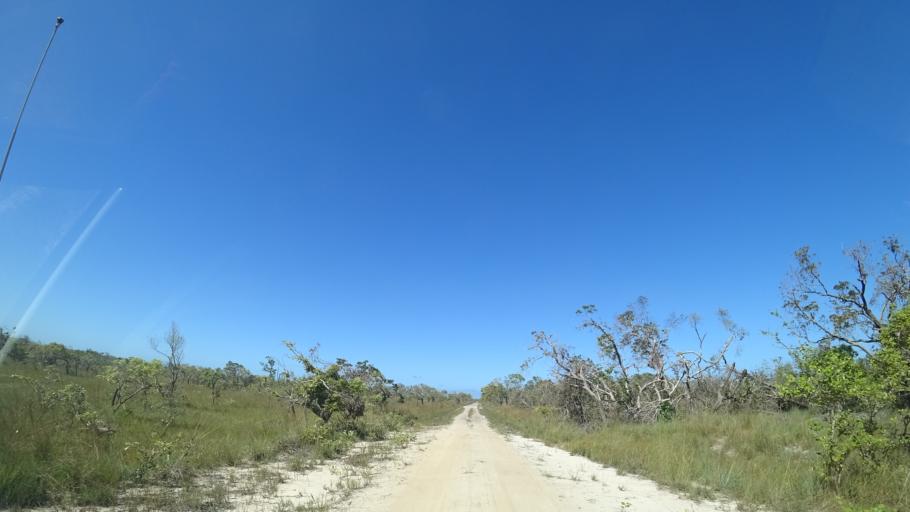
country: MZ
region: Sofala
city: Beira
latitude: -19.5722
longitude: 35.2364
